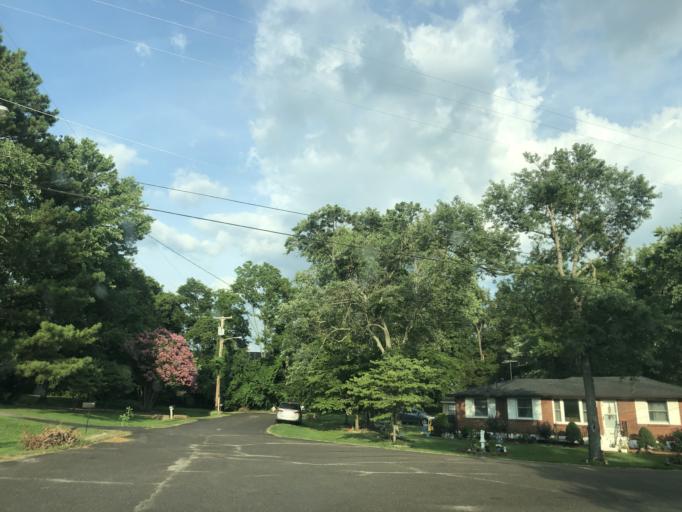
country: US
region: Tennessee
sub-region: Davidson County
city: Lakewood
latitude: 36.1544
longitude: -86.6698
